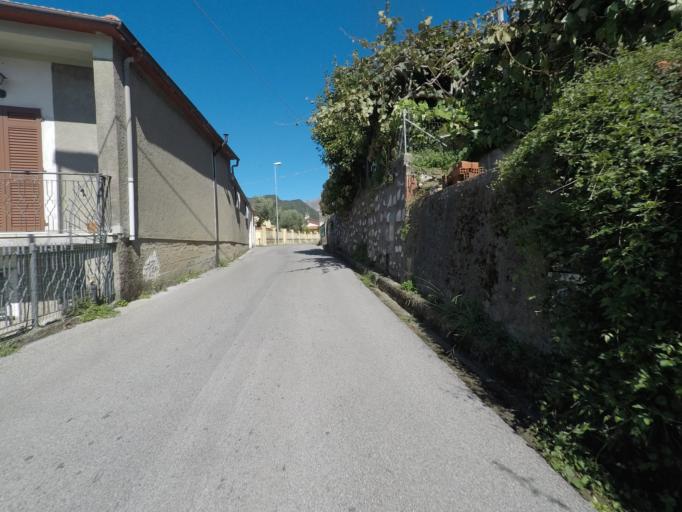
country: IT
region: Tuscany
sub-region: Provincia di Massa-Carrara
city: Montignoso
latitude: 44.0377
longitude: 10.1575
